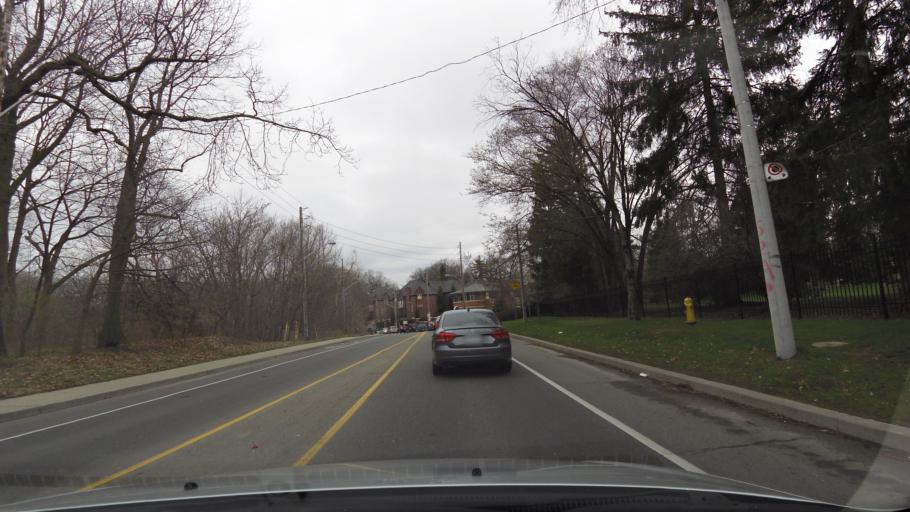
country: CA
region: Ontario
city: Toronto
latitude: 43.6952
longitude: -79.3794
